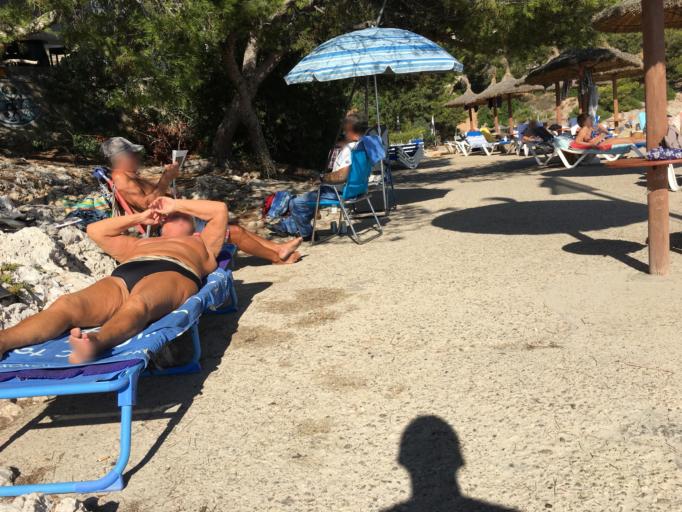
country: ES
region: Balearic Islands
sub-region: Illes Balears
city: Magaluf
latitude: 39.5341
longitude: 2.5896
